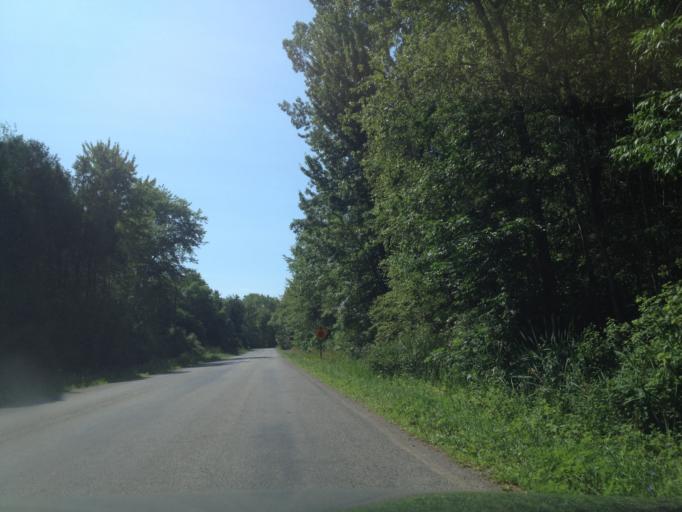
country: CA
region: Ontario
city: Norfolk County
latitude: 42.8152
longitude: -80.3769
